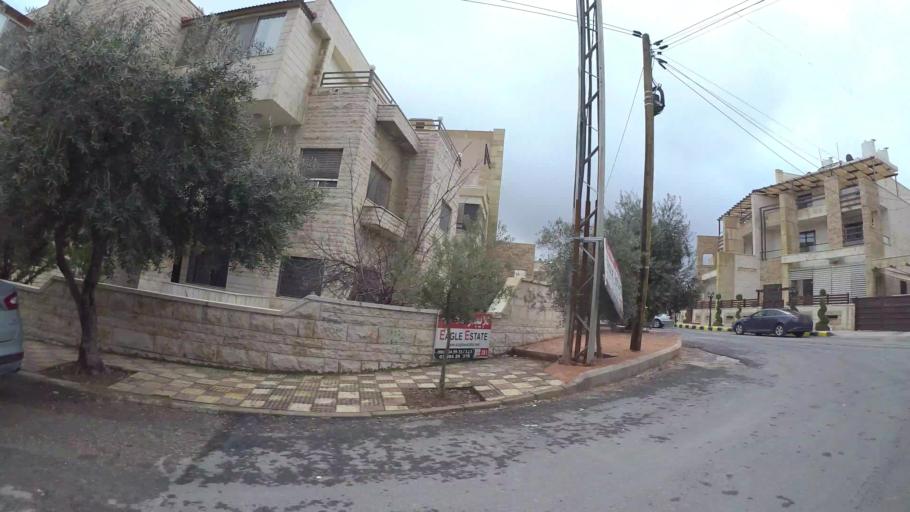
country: JO
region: Amman
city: Amman
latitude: 31.9405
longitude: 35.9051
